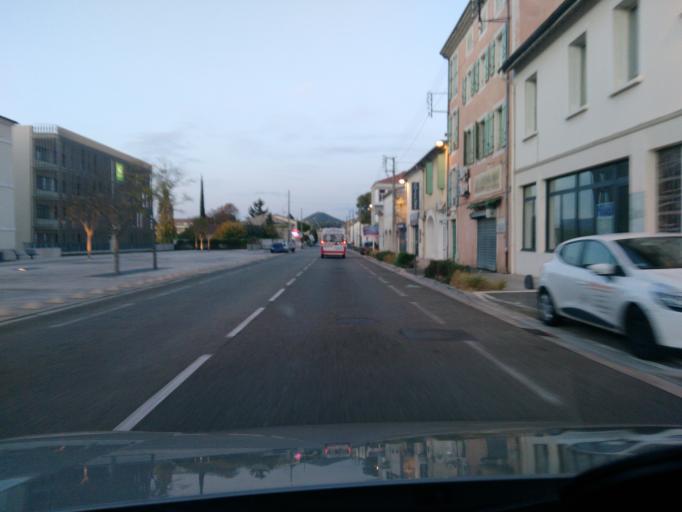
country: FR
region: Rhone-Alpes
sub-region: Departement de la Drome
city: Montelimar
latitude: 44.5619
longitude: 4.7533
